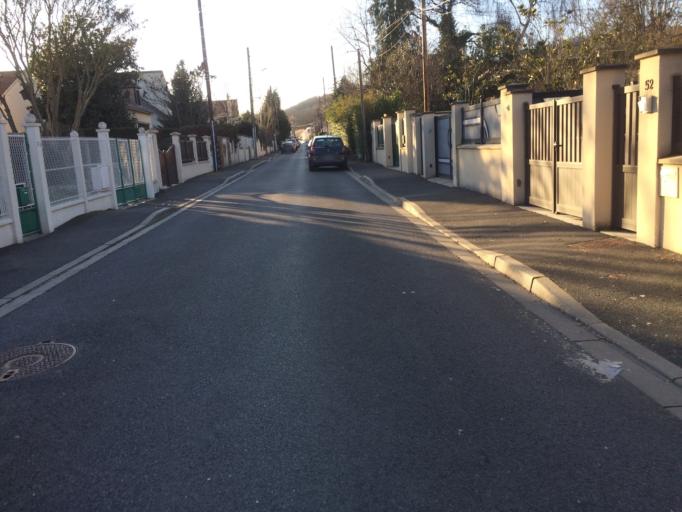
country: FR
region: Ile-de-France
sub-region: Departement de l'Essonne
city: Igny
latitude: 48.7358
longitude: 2.2241
